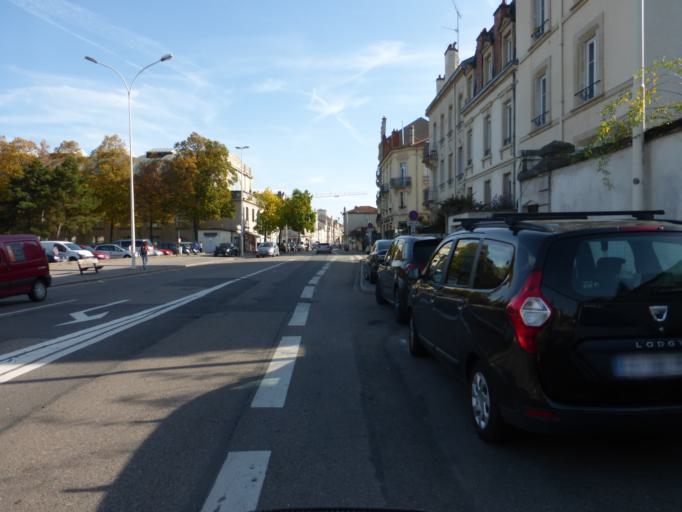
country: FR
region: Lorraine
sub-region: Departement de Meurthe-et-Moselle
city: Villers-les-Nancy
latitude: 48.6790
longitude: 6.1673
